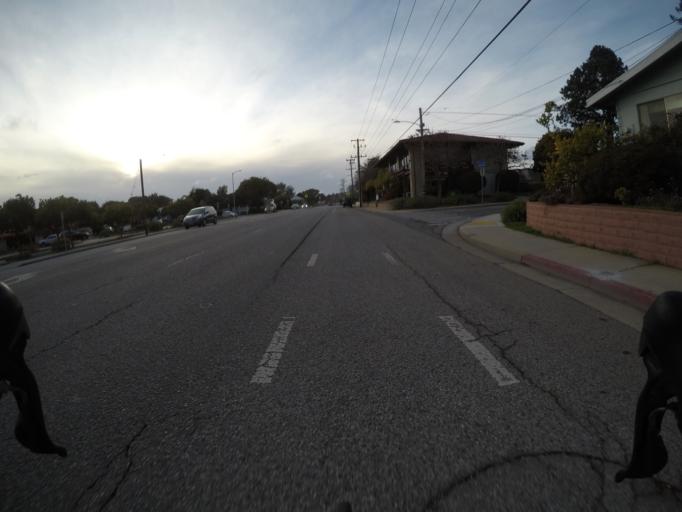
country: US
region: California
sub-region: Santa Cruz County
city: Capitola
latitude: 36.9738
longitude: -121.9618
